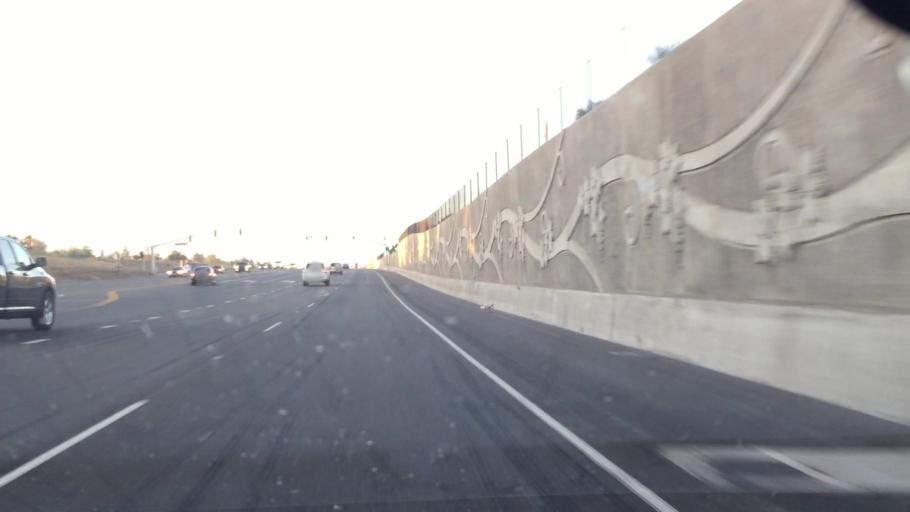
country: US
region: California
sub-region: Alameda County
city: Livermore
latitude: 37.6758
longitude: -121.8055
